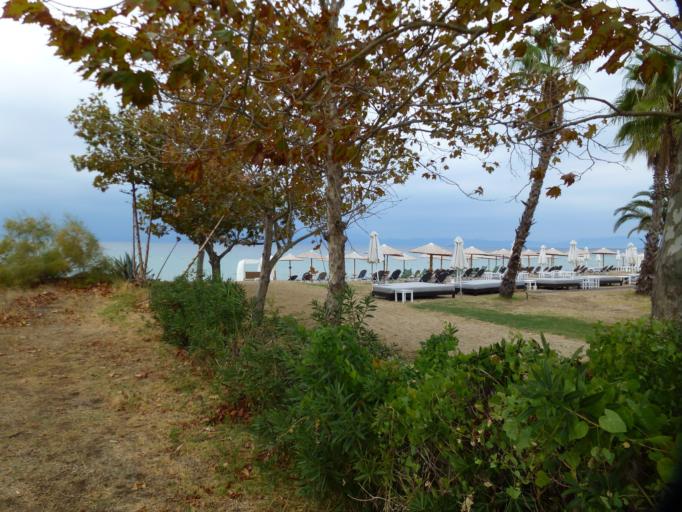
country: GR
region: East Macedonia and Thrace
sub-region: Nomos Kavalas
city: Prinos
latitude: 40.7570
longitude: 24.5618
